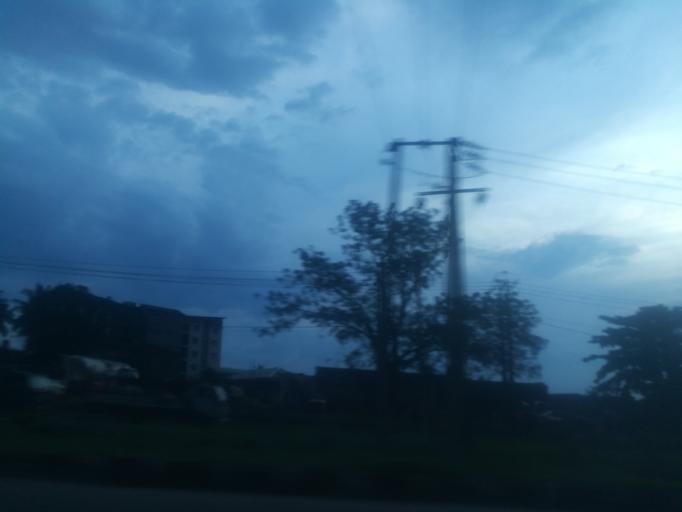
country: NG
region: Oyo
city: Ibadan
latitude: 7.3647
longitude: 3.8629
